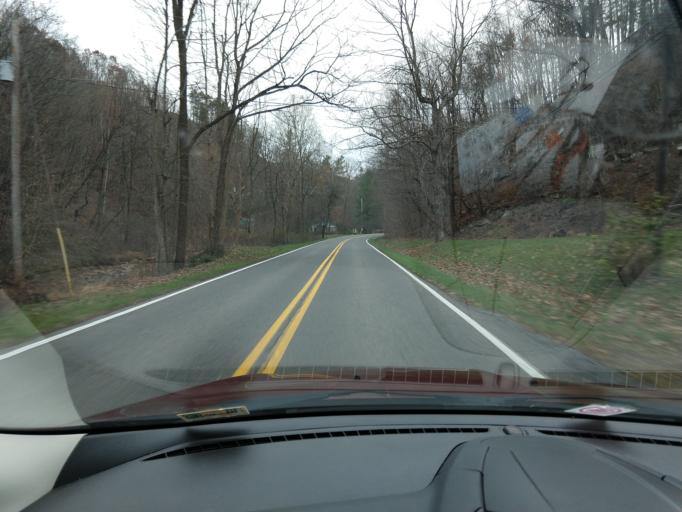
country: US
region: West Virginia
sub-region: Greenbrier County
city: White Sulphur Springs
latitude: 37.7369
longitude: -80.2252
